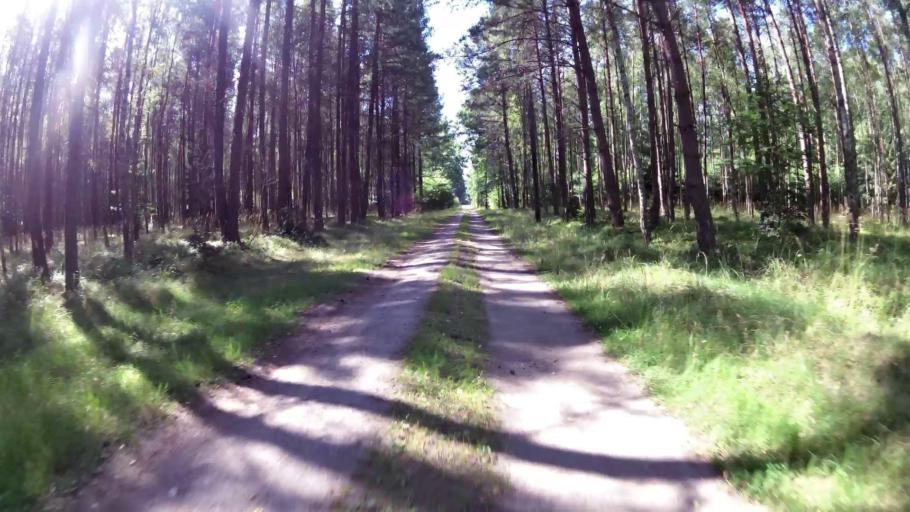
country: PL
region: West Pomeranian Voivodeship
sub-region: Powiat drawski
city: Czaplinek
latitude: 53.4041
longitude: 16.2489
